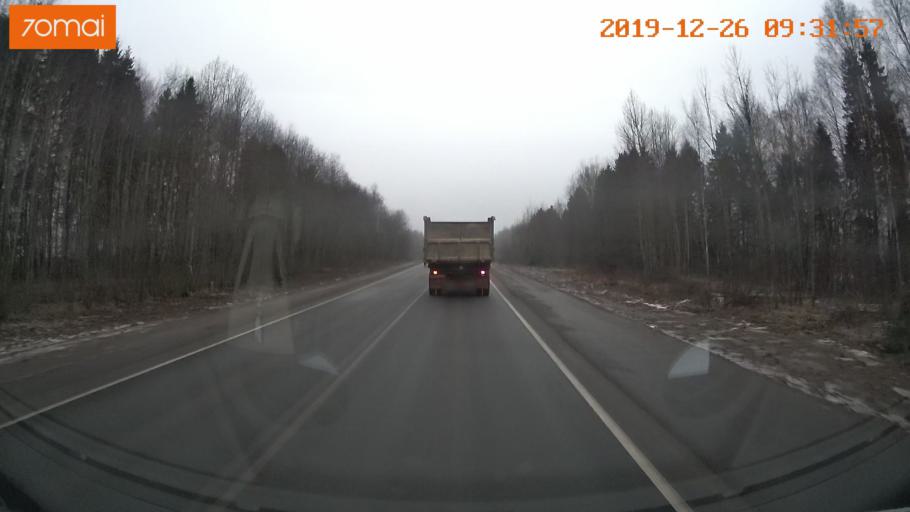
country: RU
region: Vologda
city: Gryazovets
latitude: 59.0735
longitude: 40.1222
